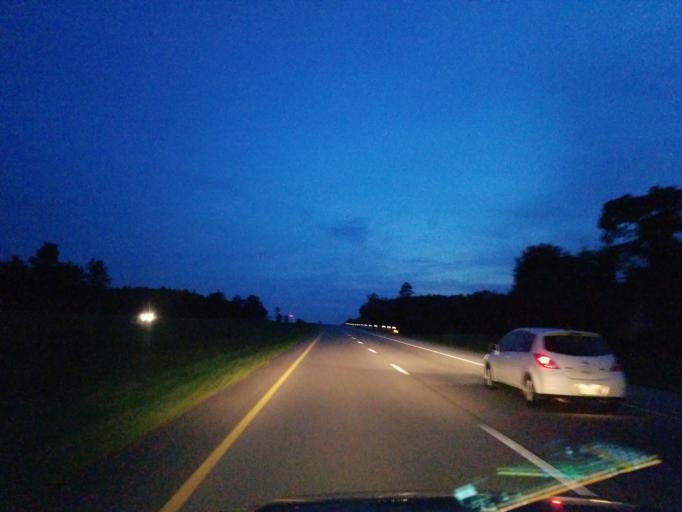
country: US
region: Mississippi
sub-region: Jones County
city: Ellisville
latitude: 31.5435
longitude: -89.2696
